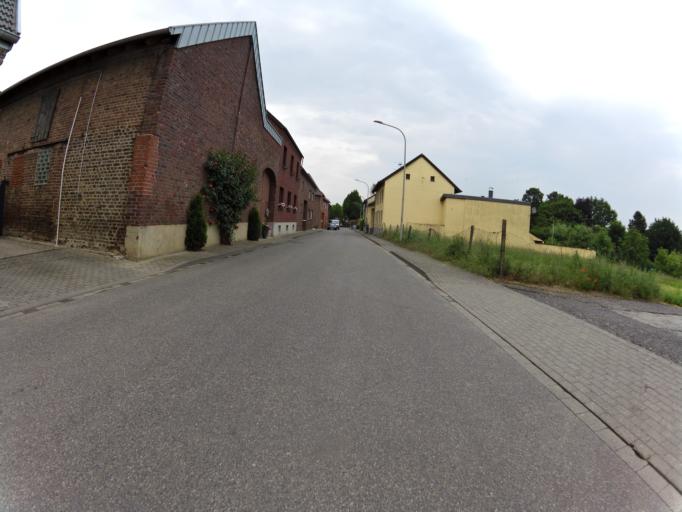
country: DE
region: North Rhine-Westphalia
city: Geilenkirchen
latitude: 50.9833
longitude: 6.1865
